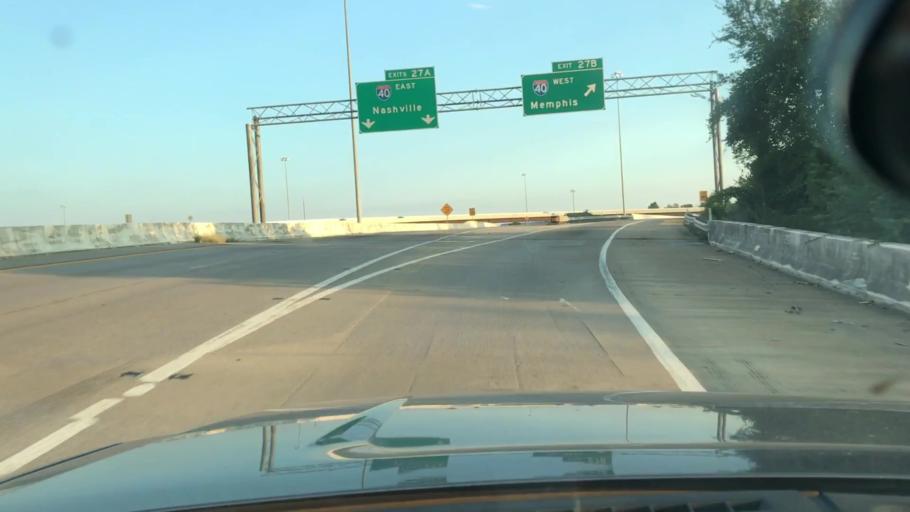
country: US
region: Tennessee
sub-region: Davidson County
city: Belle Meade
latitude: 36.1556
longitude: -86.8584
